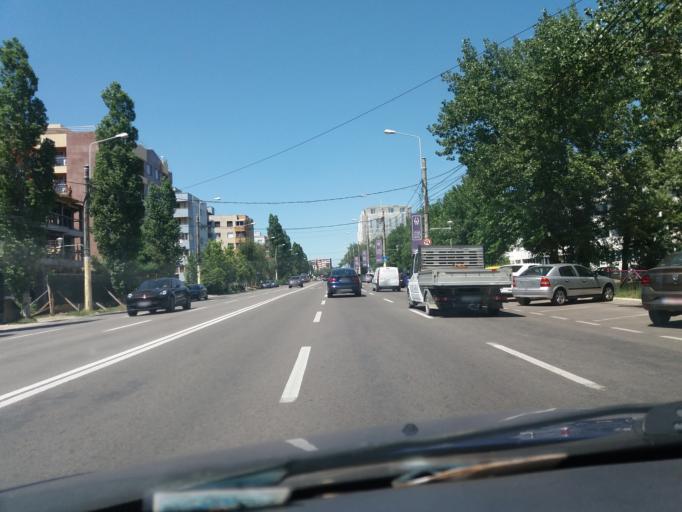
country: RO
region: Constanta
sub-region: Municipiul Constanta
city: Palazu Mare
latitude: 44.2552
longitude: 28.6188
